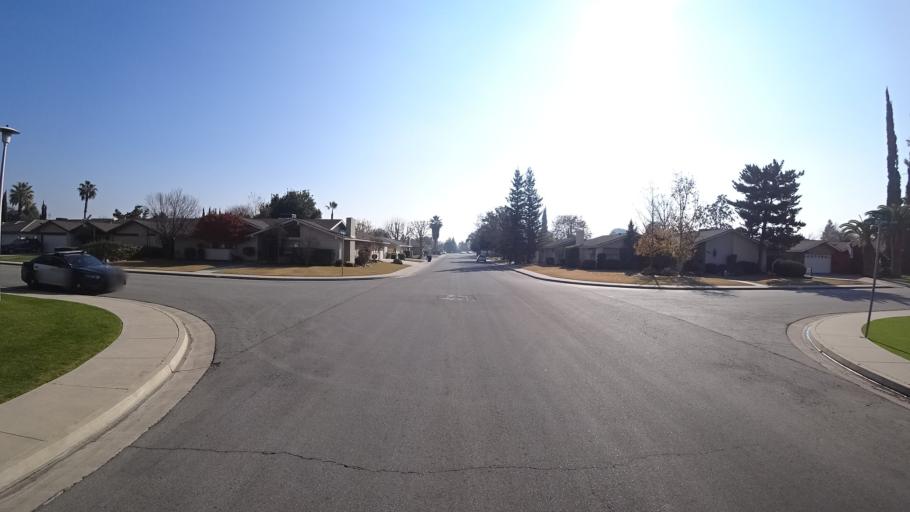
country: US
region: California
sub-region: Kern County
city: Greenacres
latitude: 35.3609
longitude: -119.0700
